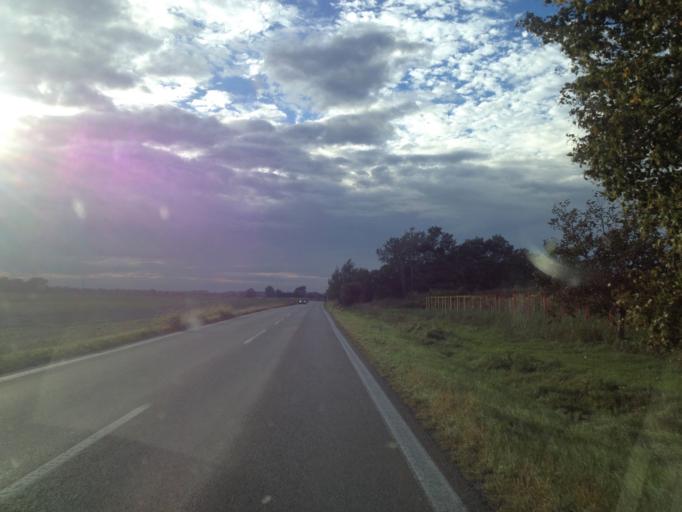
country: HU
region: Komarom-Esztergom
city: Almasfuzito
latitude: 47.7593
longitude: 18.1990
